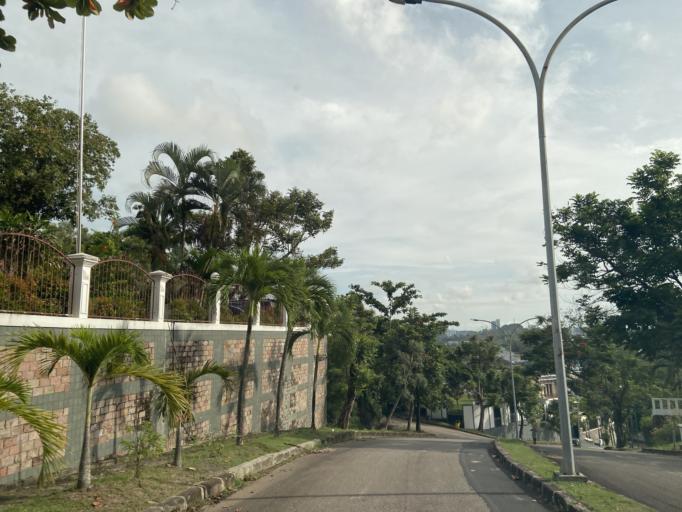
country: SG
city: Singapore
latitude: 1.1096
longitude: 104.0217
